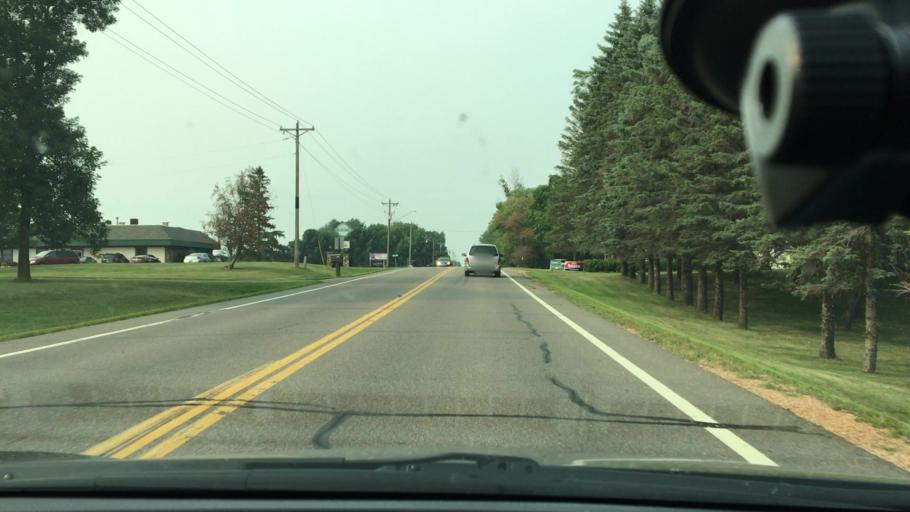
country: US
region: Minnesota
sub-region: Hennepin County
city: Osseo
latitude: 45.1585
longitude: -93.4620
